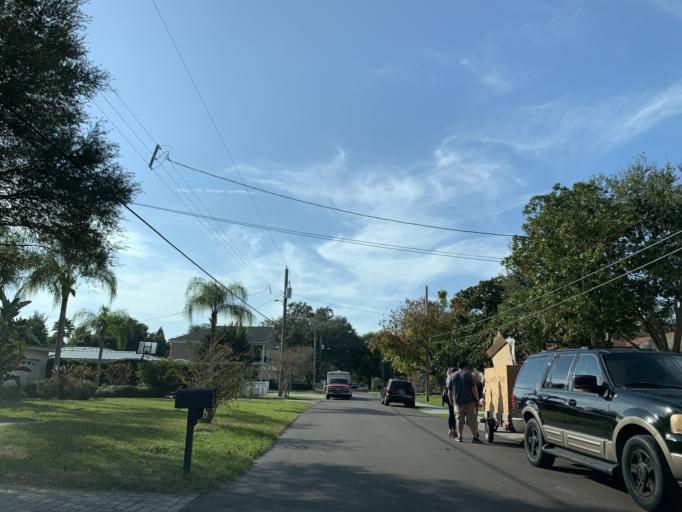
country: US
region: Florida
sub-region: Hillsborough County
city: Tampa
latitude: 27.9041
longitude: -82.4974
